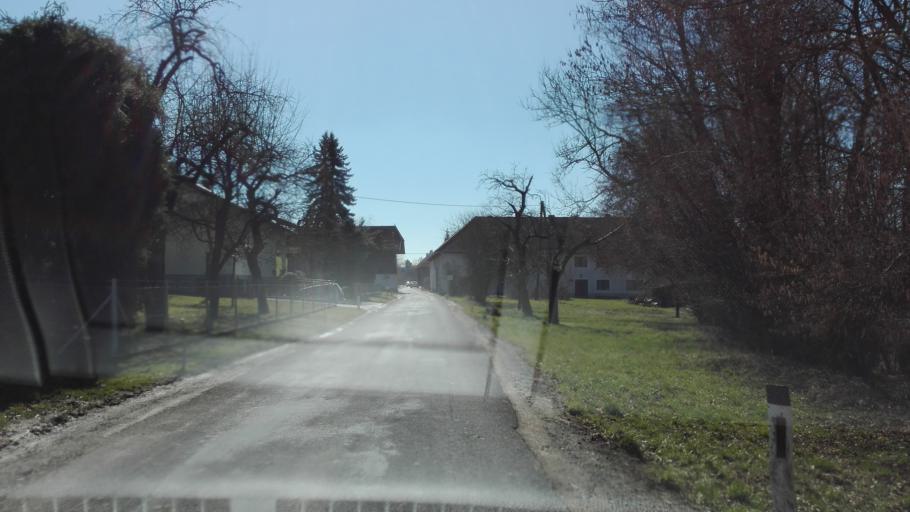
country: AT
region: Upper Austria
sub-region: Wels-Land
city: Buchkirchen
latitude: 48.2232
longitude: 13.9712
